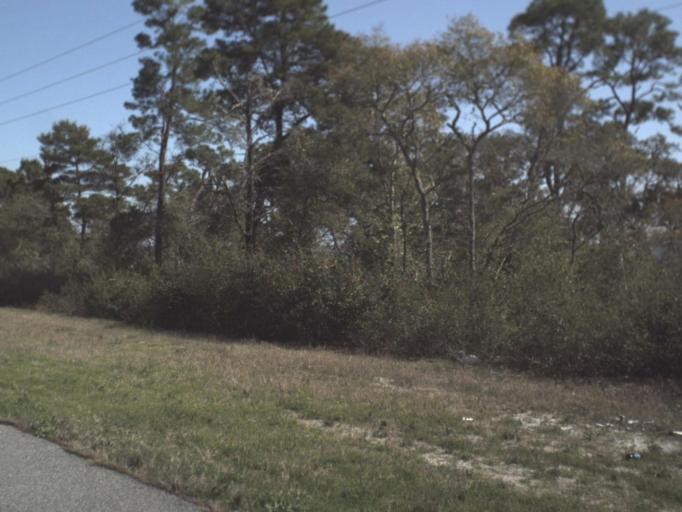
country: US
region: Florida
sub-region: Franklin County
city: Carrabelle
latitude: 29.9263
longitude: -84.4252
